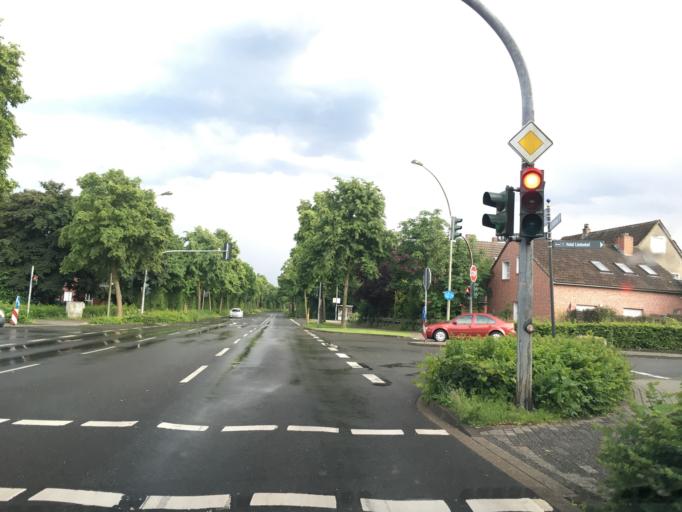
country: DE
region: North Rhine-Westphalia
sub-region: Regierungsbezirk Munster
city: Steinfurt
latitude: 52.1253
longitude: 7.3893
